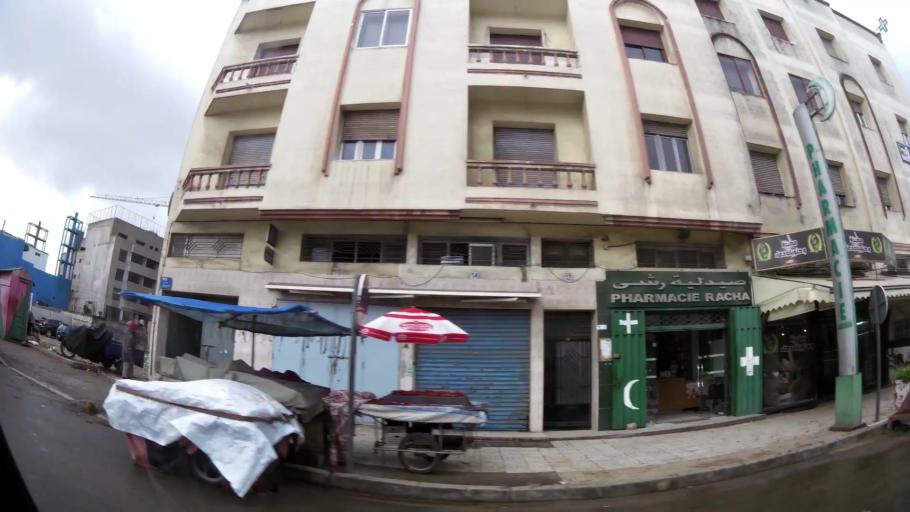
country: MA
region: Grand Casablanca
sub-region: Mediouna
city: Tit Mellil
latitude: 33.5895
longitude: -7.5262
